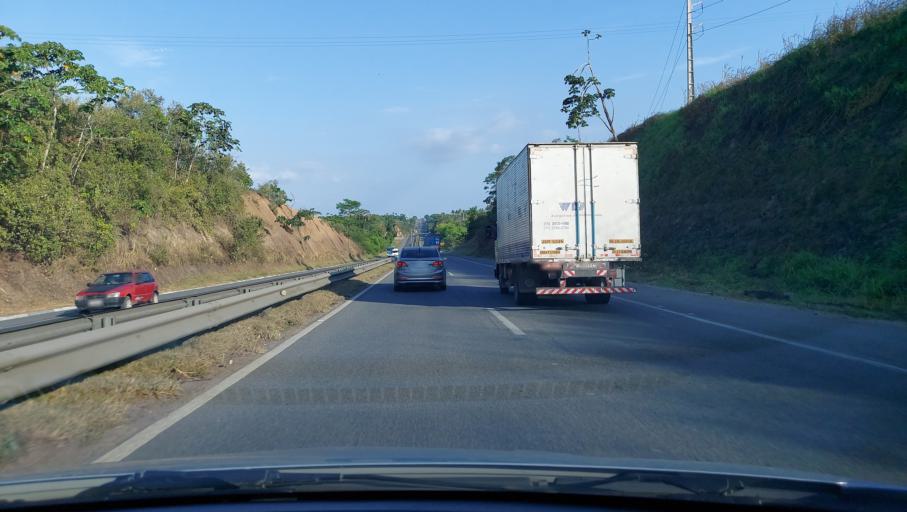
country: BR
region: Bahia
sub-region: Conceicao Do Jacuipe
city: Conceicao do Jacuipe
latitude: -12.3914
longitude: -38.7822
